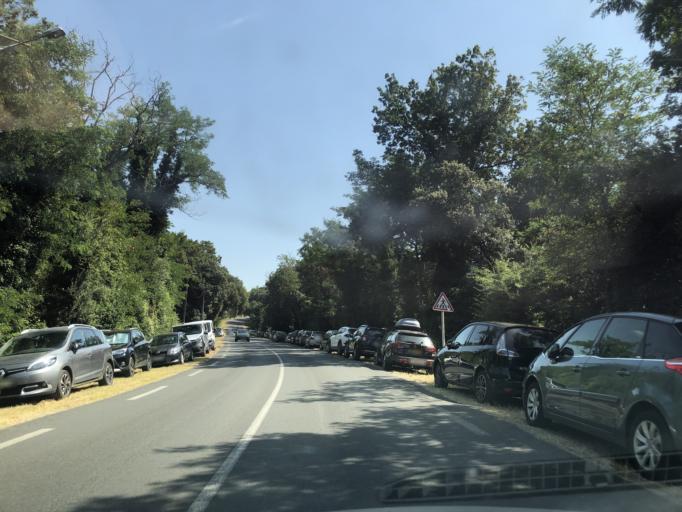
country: FR
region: Poitou-Charentes
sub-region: Departement de la Charente-Maritime
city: Meschers-sur-Gironde
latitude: 45.5677
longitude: -0.9715
